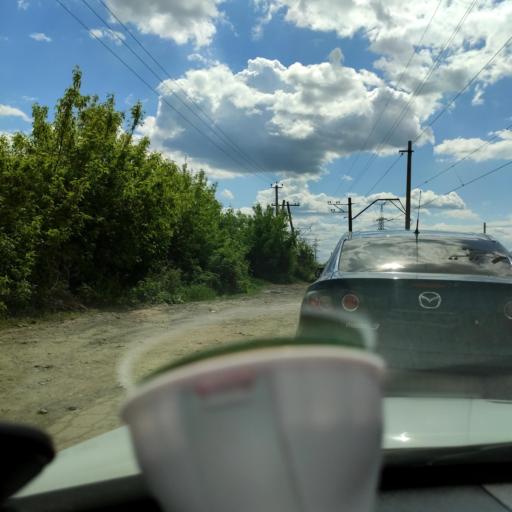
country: RU
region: Samara
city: Petra-Dubrava
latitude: 53.2689
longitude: 50.3173
